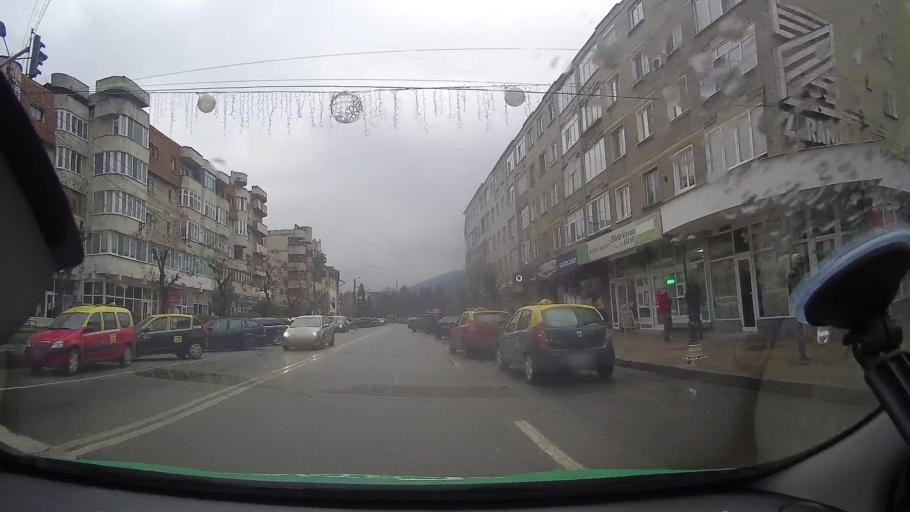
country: RO
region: Hunedoara
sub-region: Municipiul Brad
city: Brad
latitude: 46.1314
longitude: 22.7899
